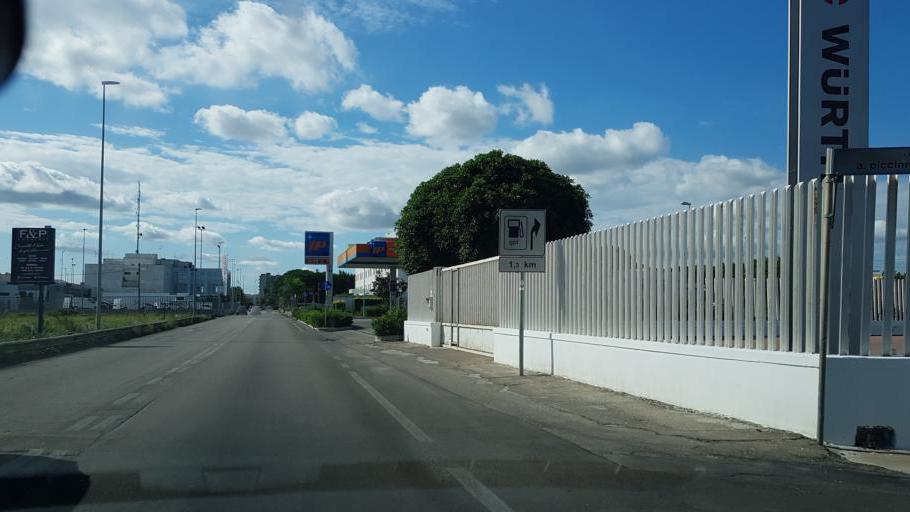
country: IT
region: Apulia
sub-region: Provincia di Lecce
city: Lecce
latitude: 40.3634
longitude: 18.1584
